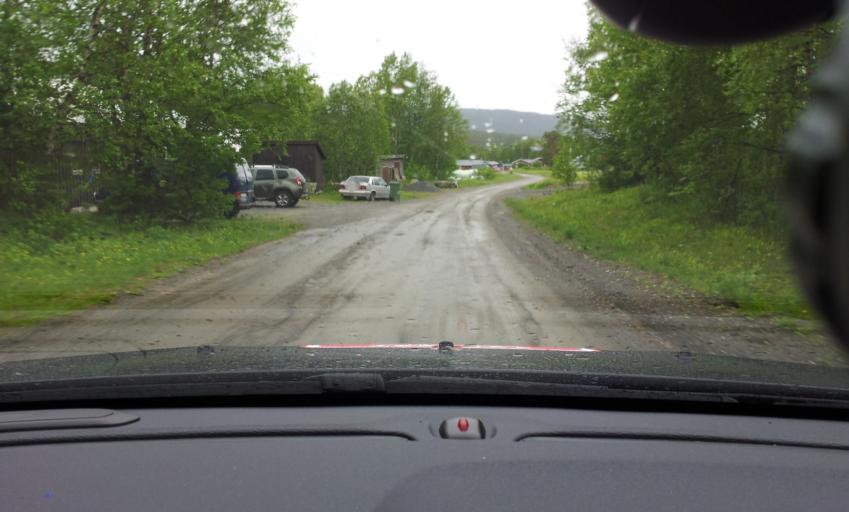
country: SE
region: Jaemtland
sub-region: Are Kommun
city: Are
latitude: 63.5086
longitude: 12.6920
